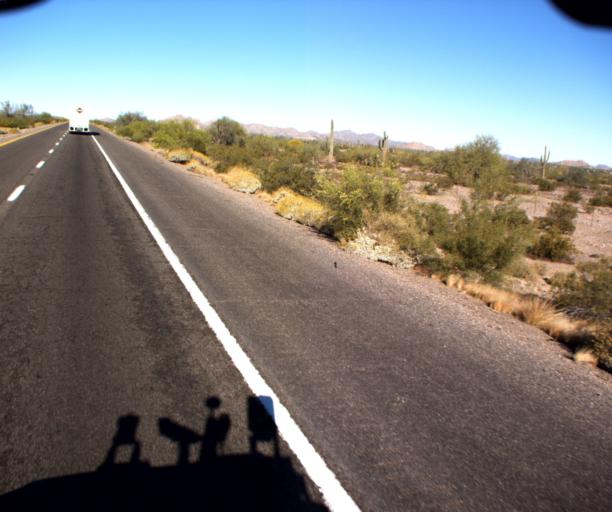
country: US
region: Arizona
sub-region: Pinal County
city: Maricopa
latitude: 32.8318
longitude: -112.0536
